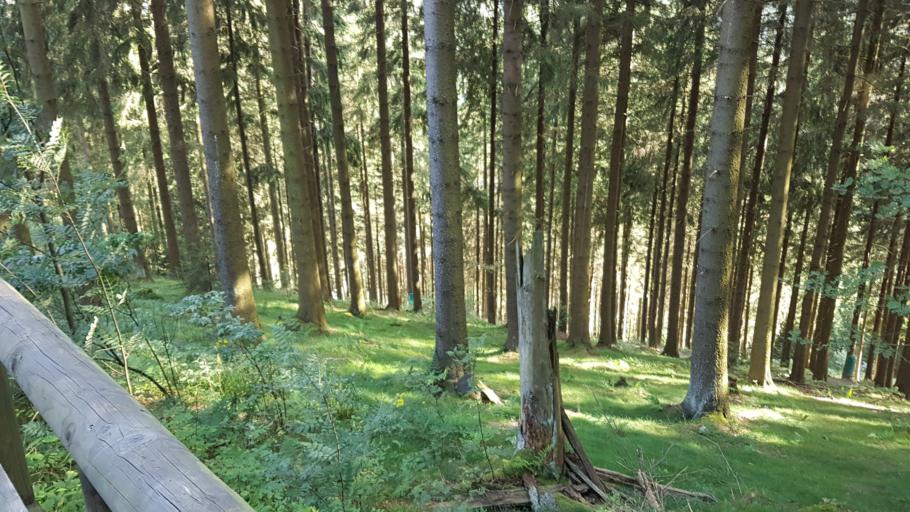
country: DE
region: North Rhine-Westphalia
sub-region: Regierungsbezirk Arnsberg
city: Winterberg
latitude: 51.1809
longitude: 8.5075
